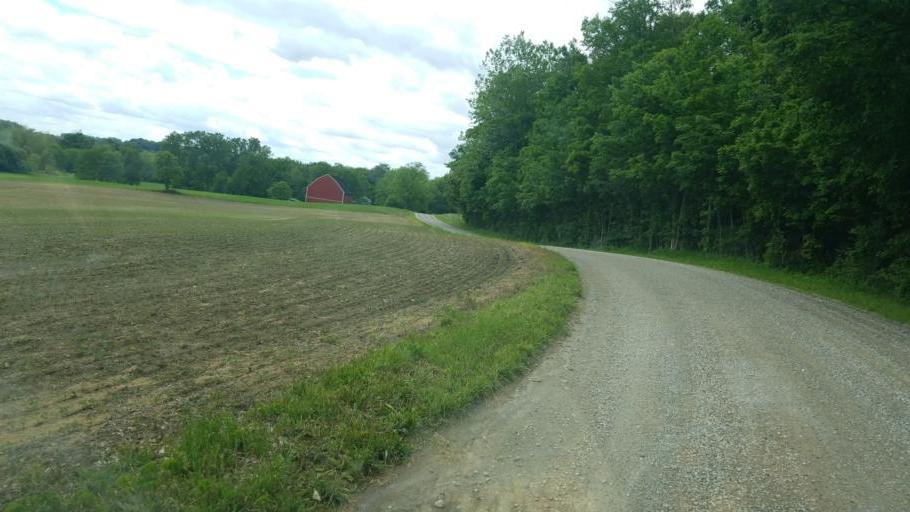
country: US
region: Ohio
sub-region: Richland County
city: Lexington
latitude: 40.6431
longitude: -82.6716
